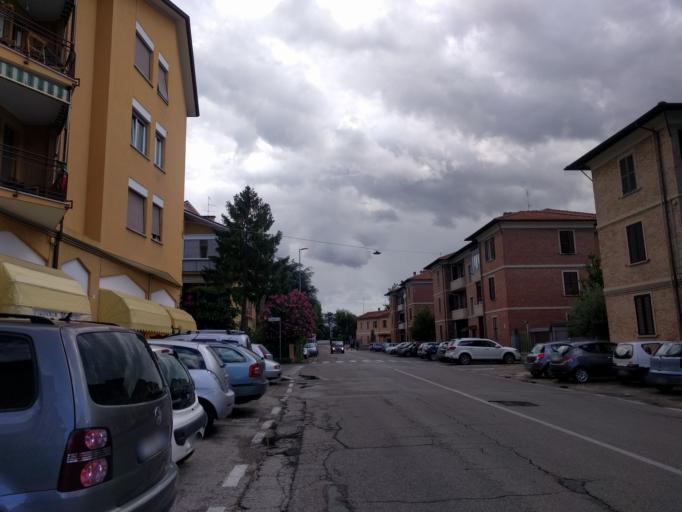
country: IT
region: The Marches
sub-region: Provincia di Pesaro e Urbino
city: Pesaro
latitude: 43.8988
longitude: 12.9079
